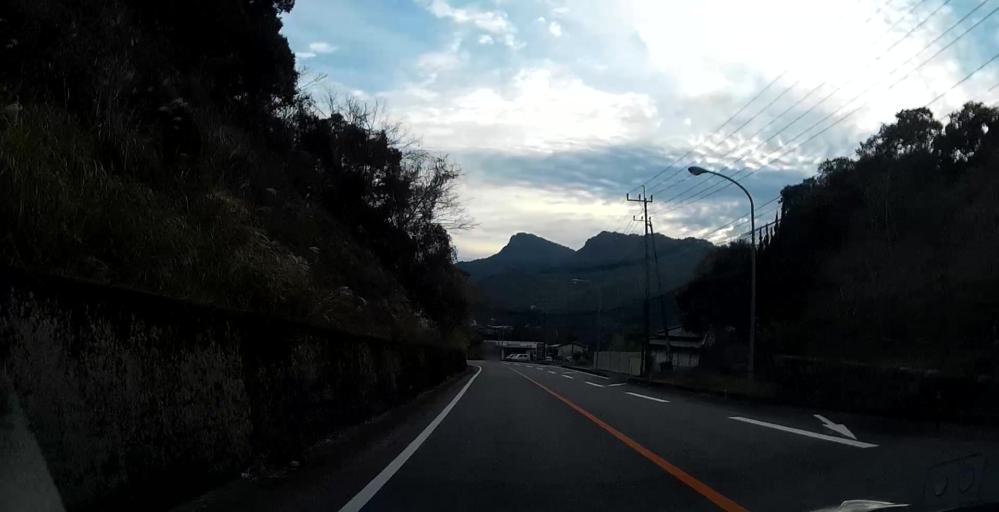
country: JP
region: Kumamoto
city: Yatsushiro
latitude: 32.4962
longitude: 130.4201
